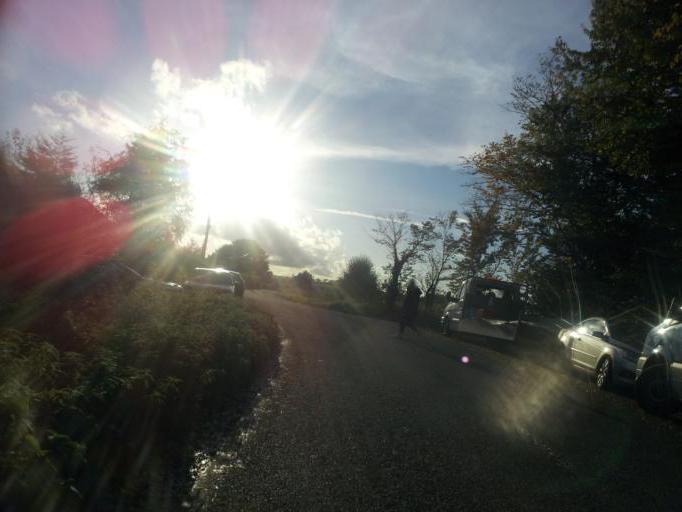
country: GB
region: England
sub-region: Kent
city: Sittingbourne
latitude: 51.3750
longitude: 0.7052
